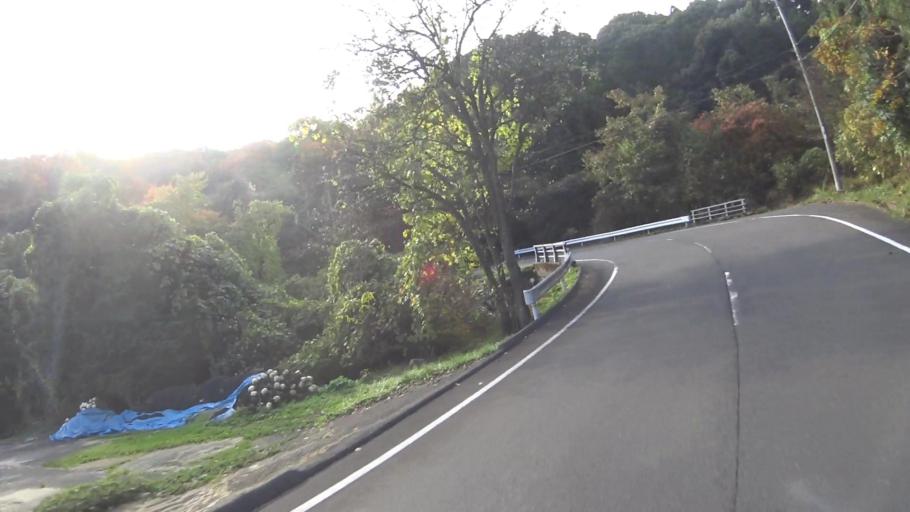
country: JP
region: Kyoto
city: Maizuru
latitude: 35.5492
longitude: 135.3950
